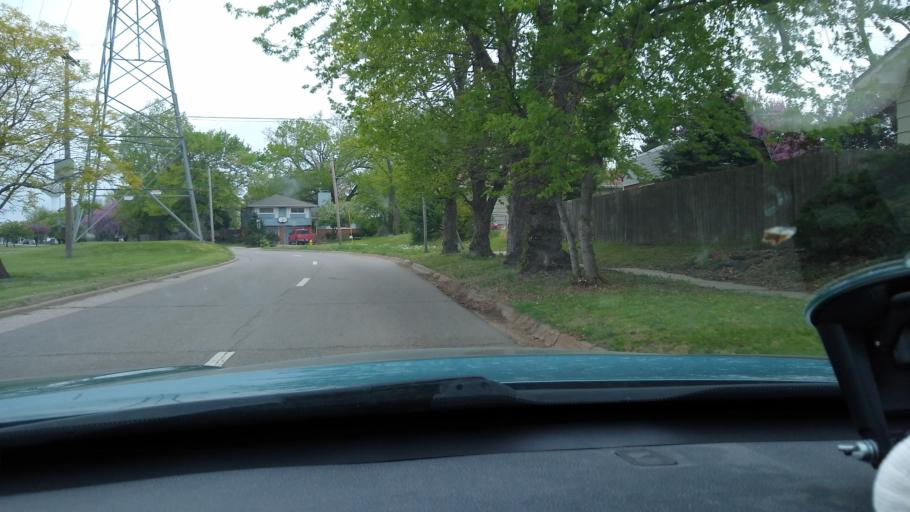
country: US
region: Kansas
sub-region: Saline County
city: Salina
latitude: 38.8014
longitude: -97.6014
